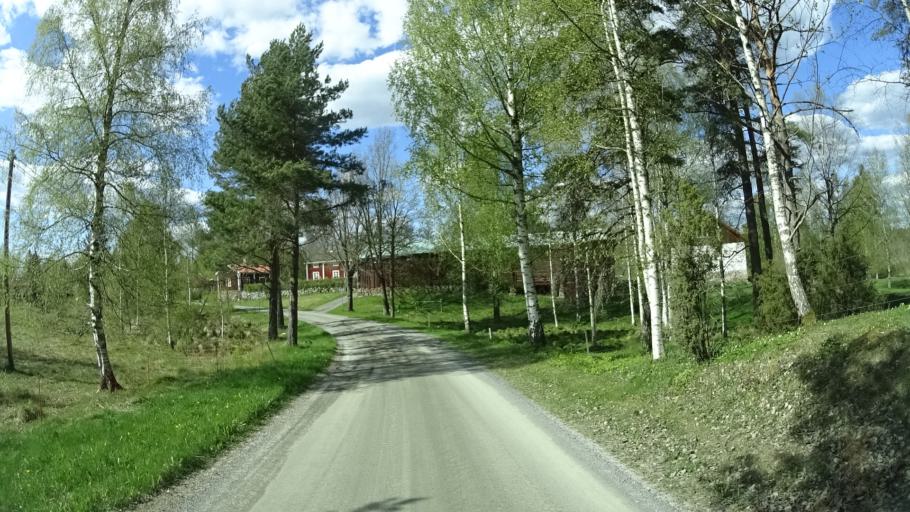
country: SE
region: OErebro
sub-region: Nora Kommun
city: As
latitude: 59.4436
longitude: 14.8170
